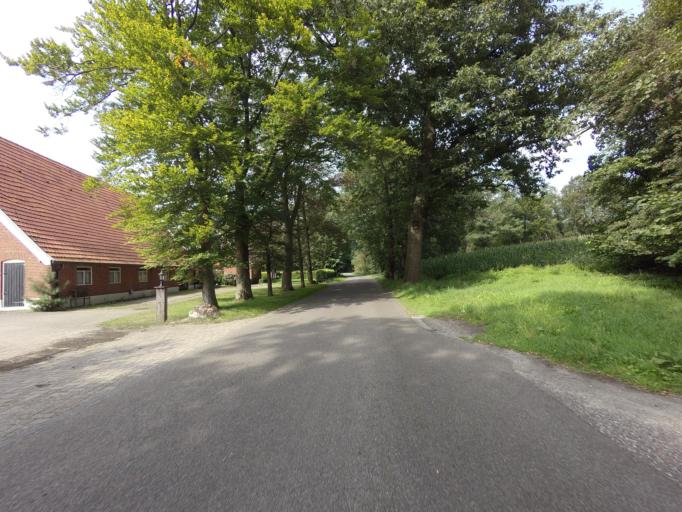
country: DE
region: Lower Saxony
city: Getelo
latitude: 52.4308
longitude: 6.9050
